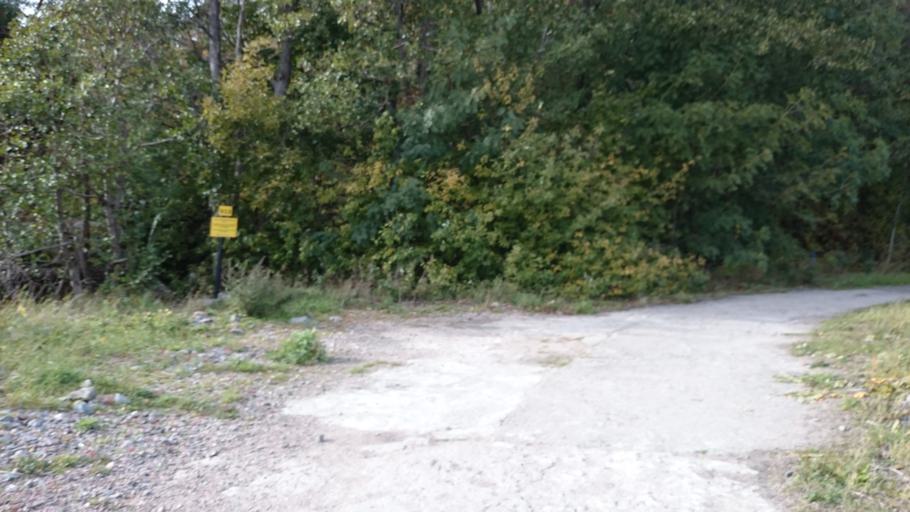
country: FI
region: Uusimaa
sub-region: Helsinki
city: Helsinki
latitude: 60.1346
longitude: 25.0103
